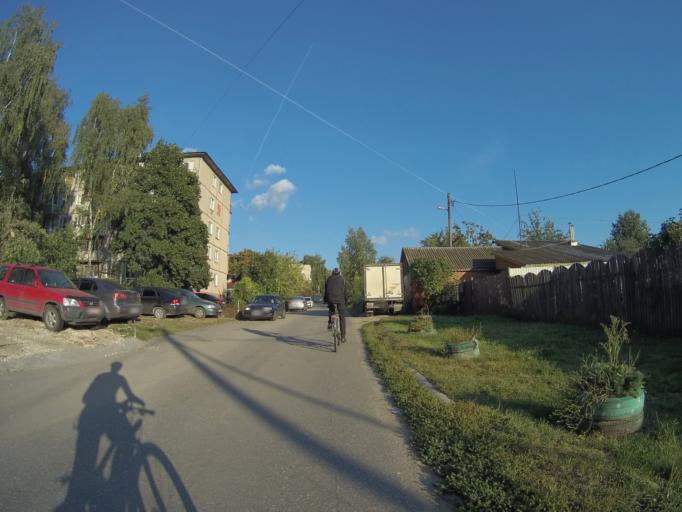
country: RU
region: Vladimir
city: Vladimir
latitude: 56.1467
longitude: 40.3622
